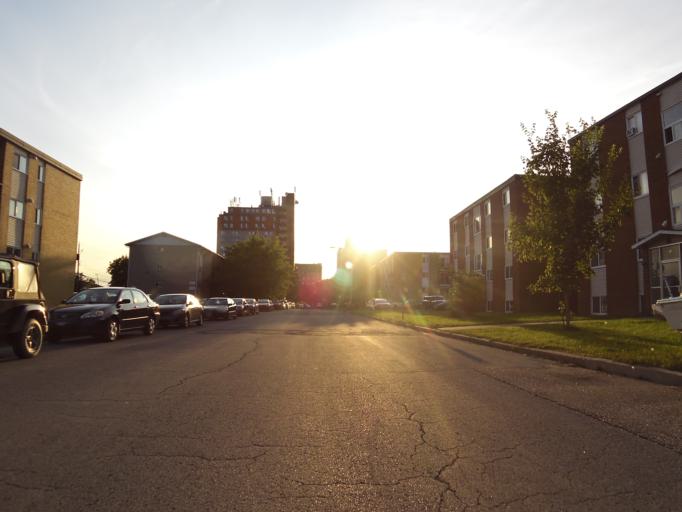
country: CA
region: Quebec
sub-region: Outaouais
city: Gatineau
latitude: 45.4664
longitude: -75.6953
